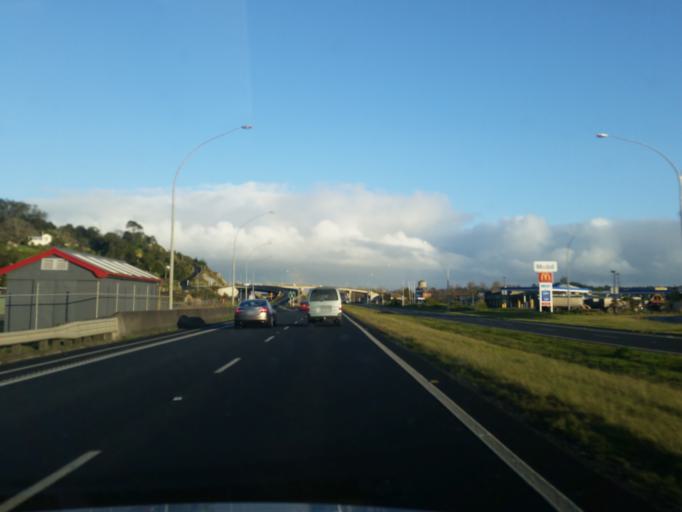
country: NZ
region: Auckland
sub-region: Auckland
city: Pukekohe East
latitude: -37.2759
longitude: 175.0470
